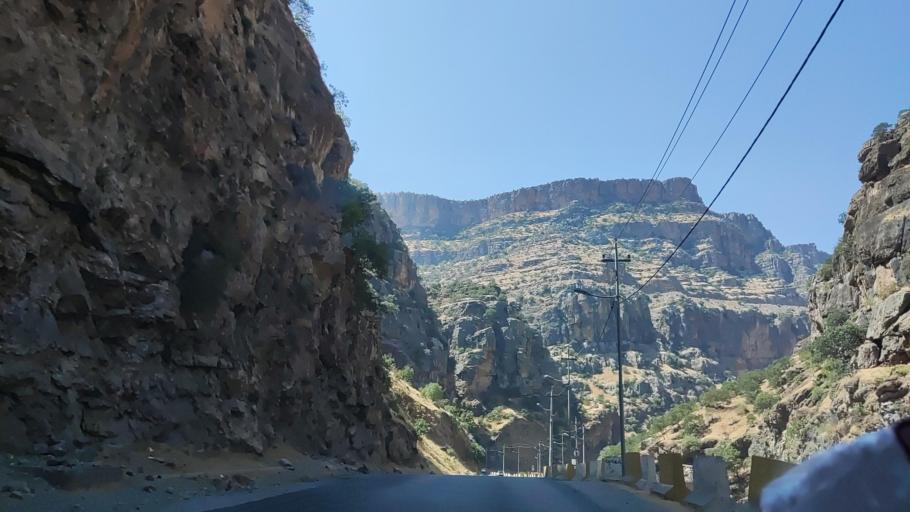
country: IQ
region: Arbil
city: Ruwandiz
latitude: 36.6344
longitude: 44.4911
